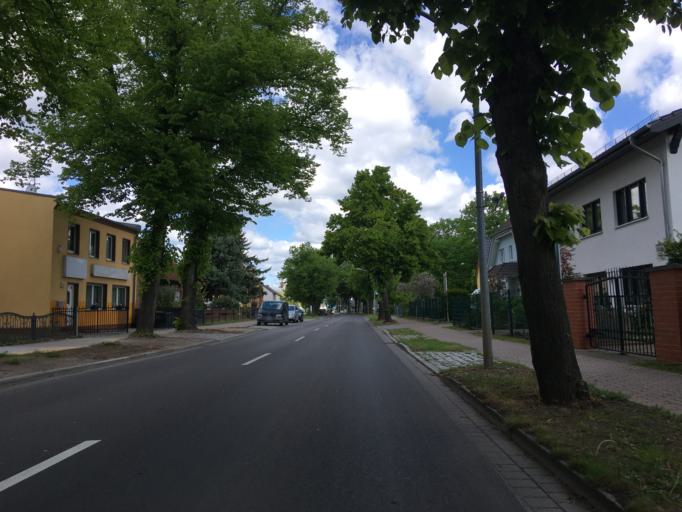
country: DE
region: Brandenburg
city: Oranienburg
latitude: 52.7637
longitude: 13.2547
